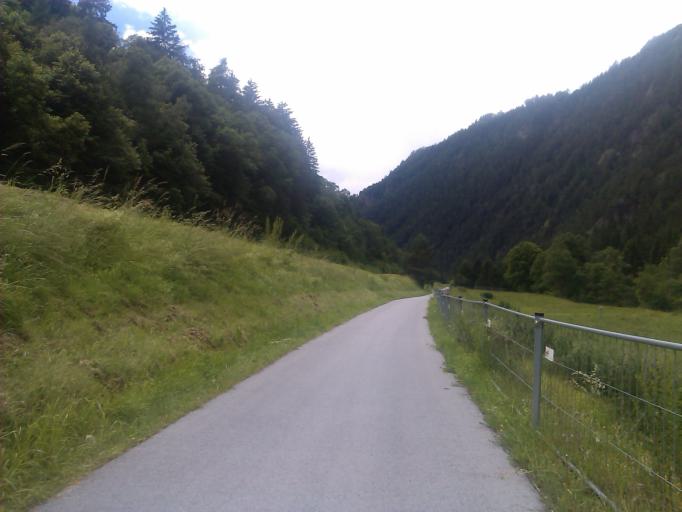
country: AT
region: Tyrol
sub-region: Politischer Bezirk Landeck
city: Ried im Oberinntal
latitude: 47.0443
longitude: 10.6387
